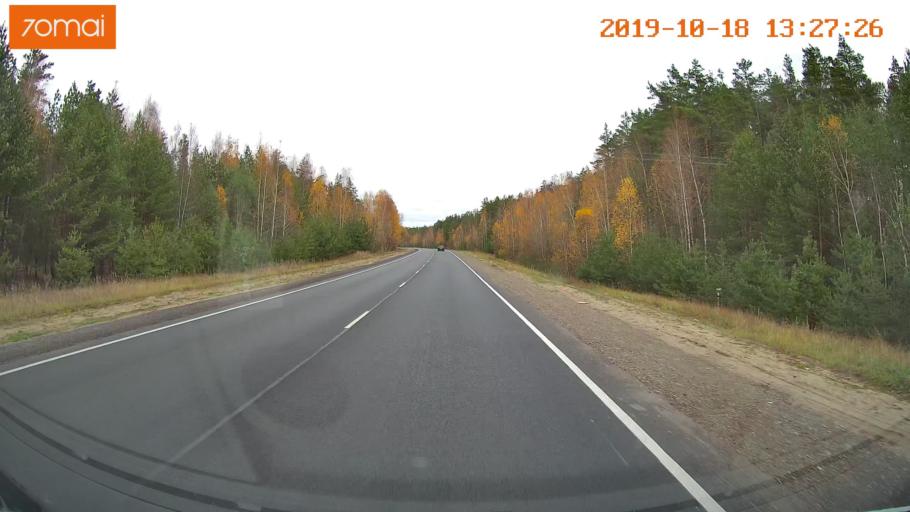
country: RU
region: Rjazan
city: Solotcha
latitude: 54.7637
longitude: 39.8546
